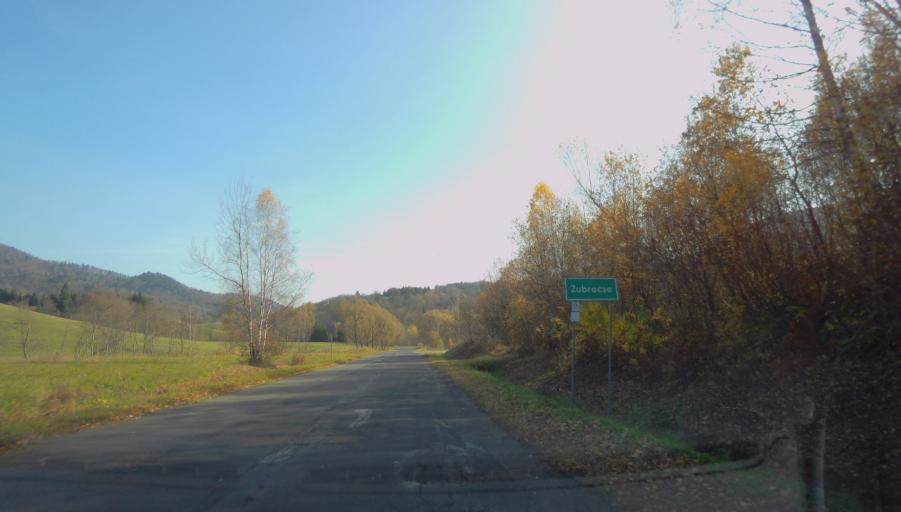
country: PL
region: Subcarpathian Voivodeship
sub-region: Powiat leski
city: Cisna
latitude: 49.2067
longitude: 22.2556
